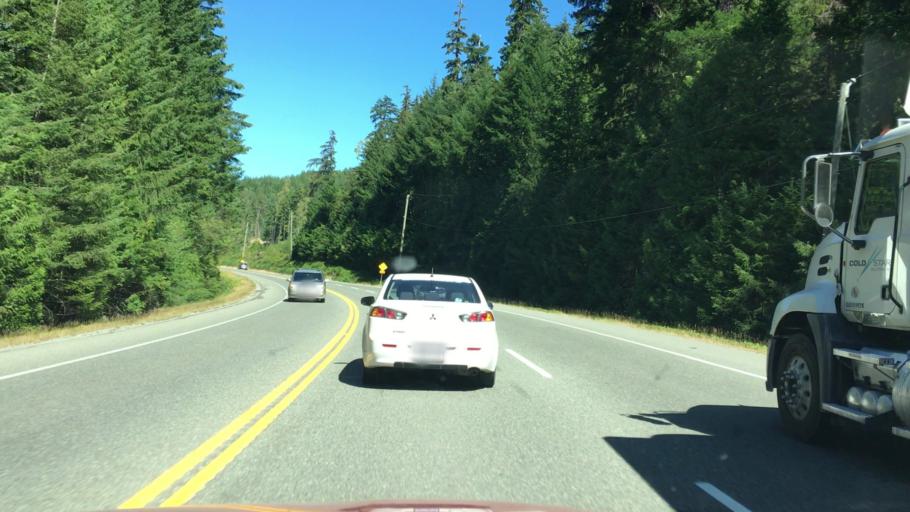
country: CA
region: British Columbia
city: Port Alberni
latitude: 49.2937
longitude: -124.5668
